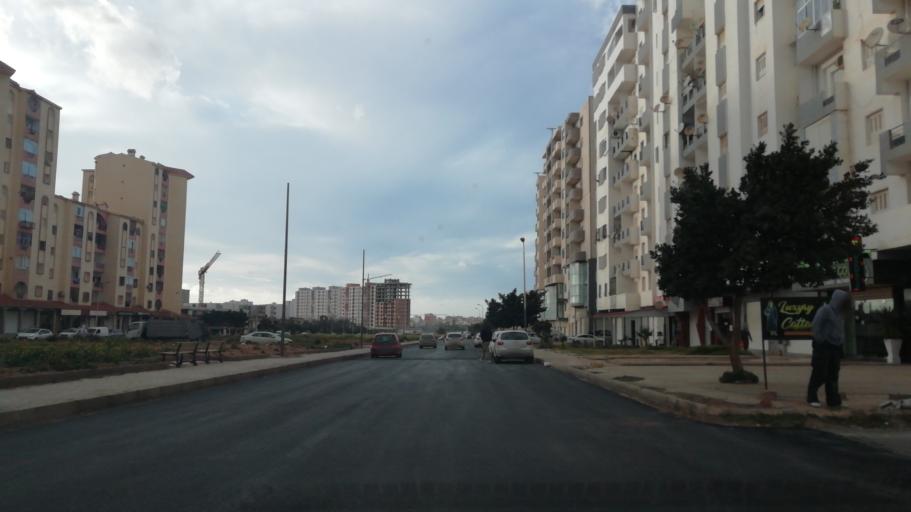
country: DZ
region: Oran
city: Bir el Djir
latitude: 35.7103
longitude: -0.5668
